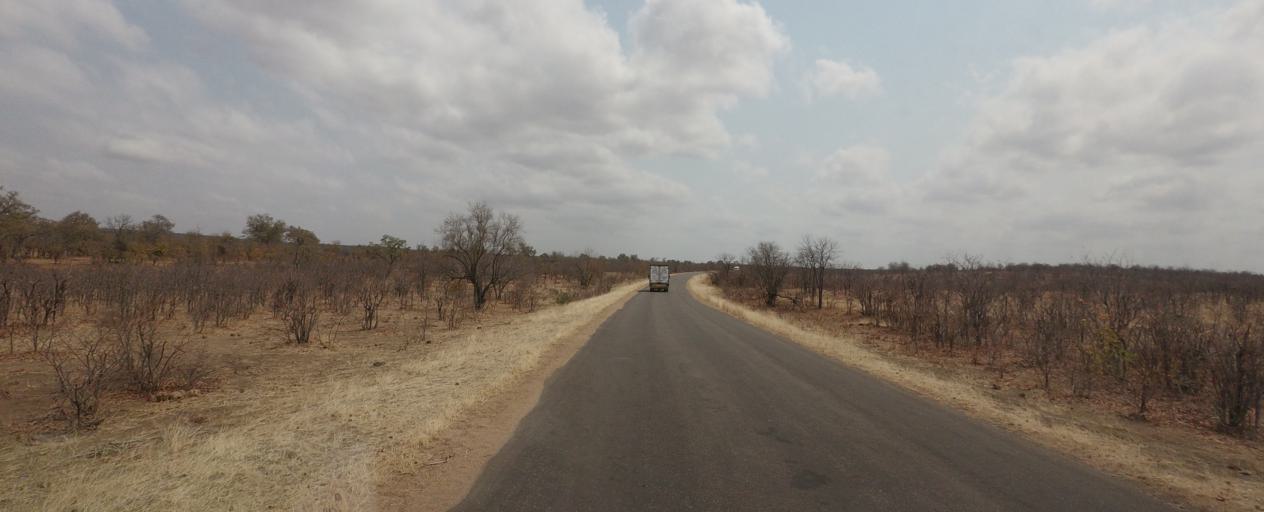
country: ZA
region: Limpopo
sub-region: Mopani District Municipality
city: Phalaborwa
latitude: -23.6088
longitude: 31.4554
